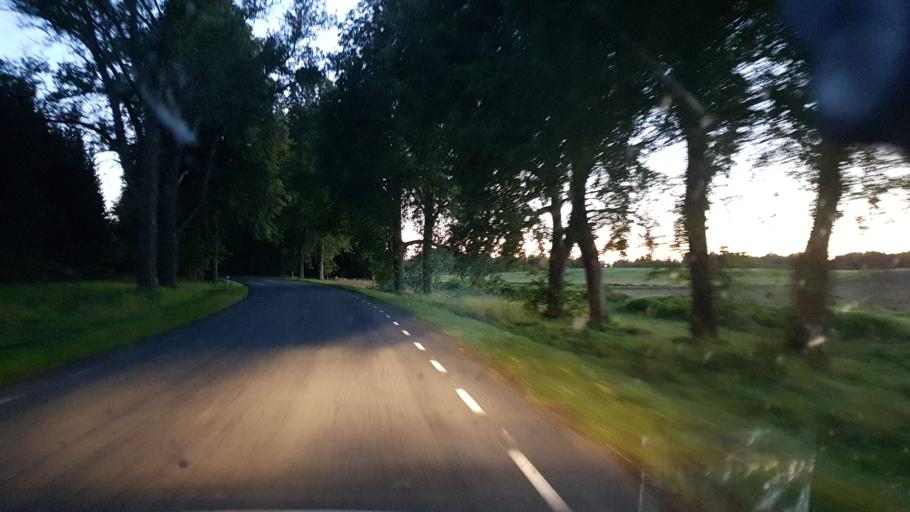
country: LV
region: Apes Novads
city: Ape
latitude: 57.6197
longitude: 26.5941
